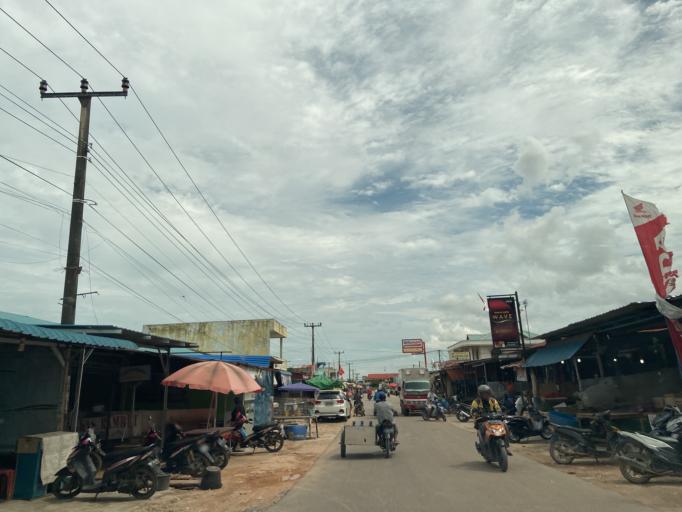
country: SG
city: Singapore
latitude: 1.0324
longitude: 103.9761
